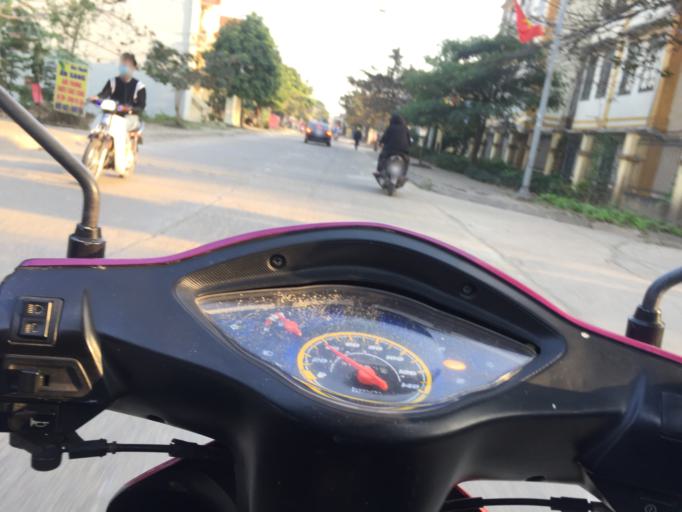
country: VN
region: Ha Noi
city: Chuc Son
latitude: 20.9198
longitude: 105.7128
